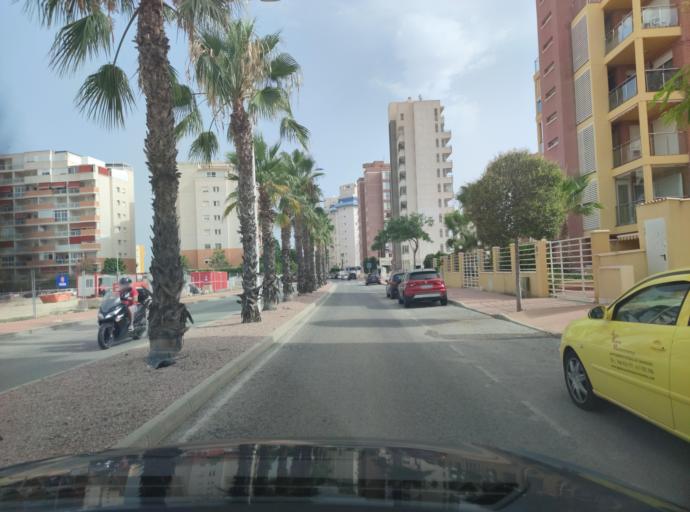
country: ES
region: Valencia
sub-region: Provincia de Alicante
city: Guardamar del Segura
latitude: 38.0993
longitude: -0.6557
